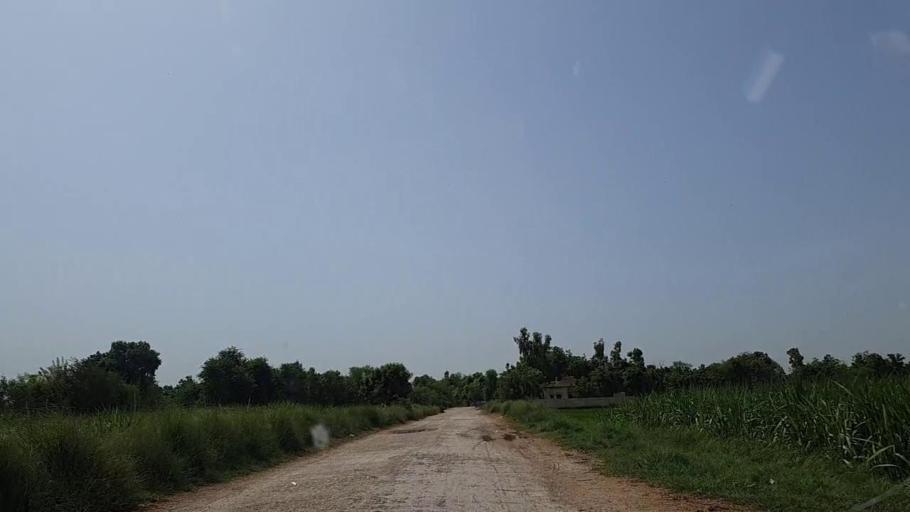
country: PK
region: Sindh
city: Naushahro Firoz
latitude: 26.8322
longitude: 68.0199
